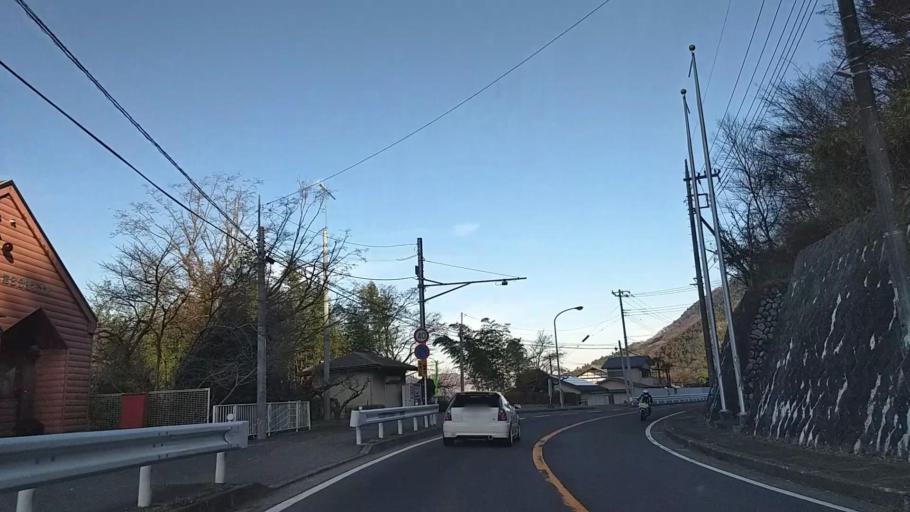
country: JP
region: Yamanashi
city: Uenohara
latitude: 35.5491
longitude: 139.1461
